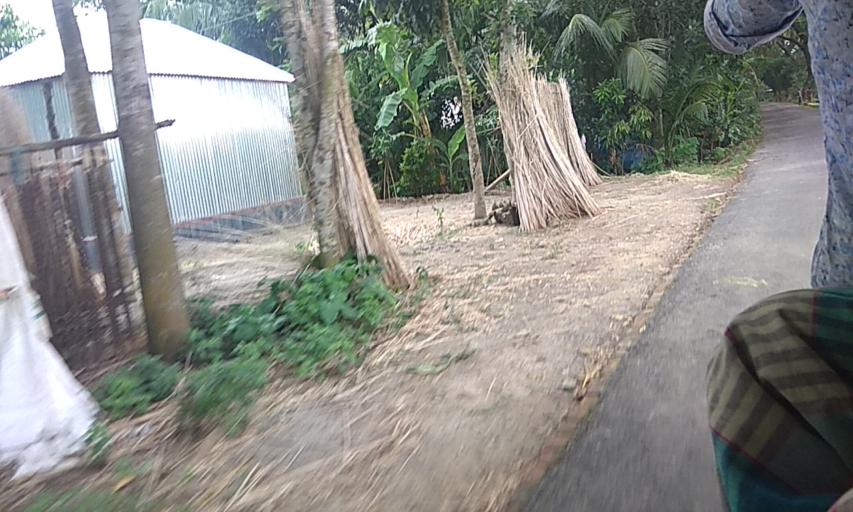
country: BD
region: Dhaka
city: Dohar
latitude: 23.4755
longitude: 90.0566
